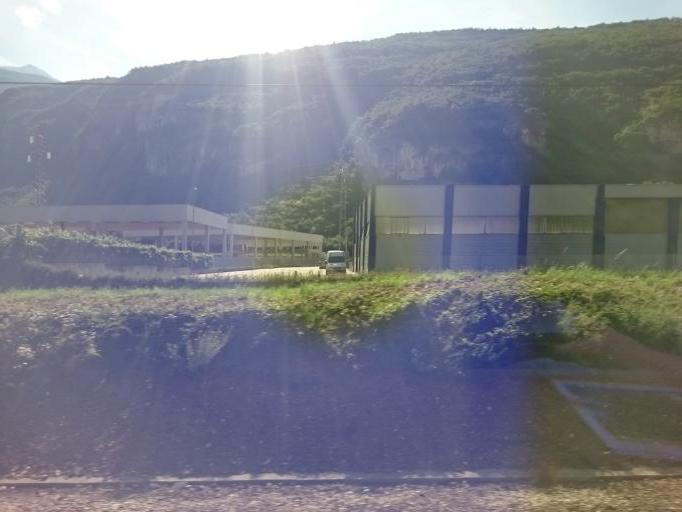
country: IT
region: Trentino-Alto Adige
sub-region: Provincia di Trento
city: Ala
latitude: 45.7756
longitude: 11.0133
